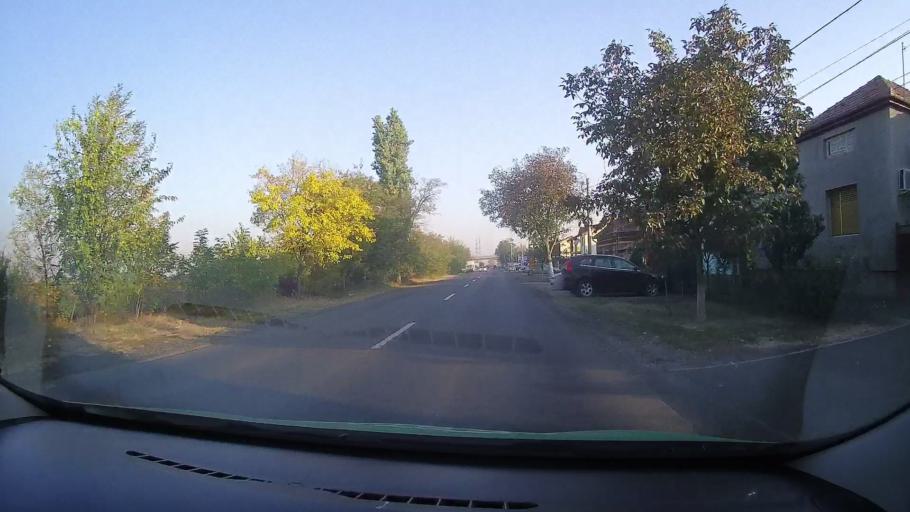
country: RO
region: Arad
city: Arad
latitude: 46.2139
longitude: 21.3206
